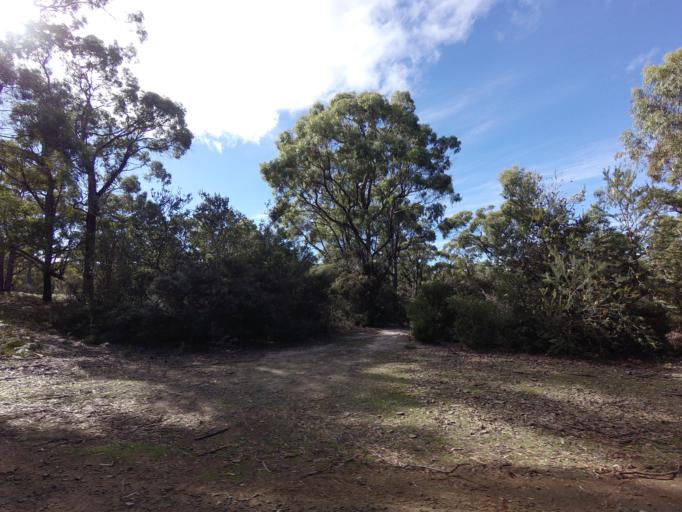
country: AU
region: Tasmania
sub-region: Clarence
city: Sandford
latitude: -42.9769
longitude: 147.7166
